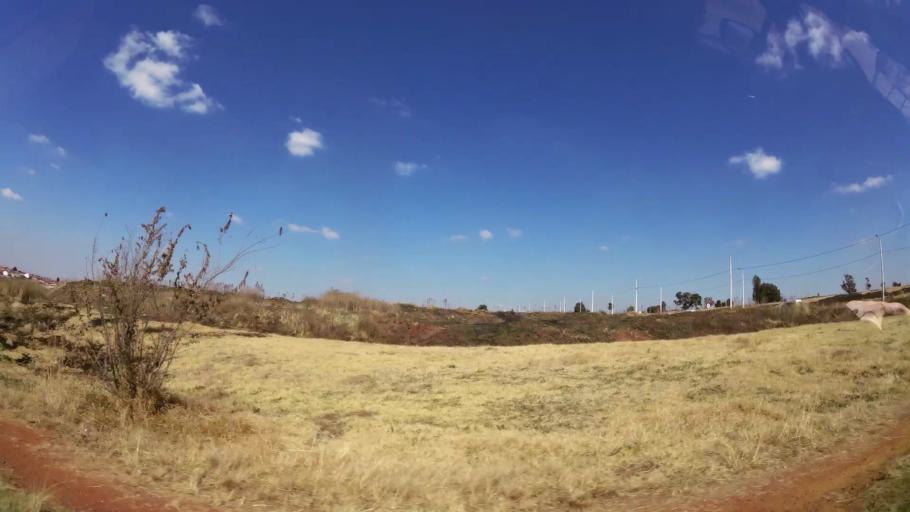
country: ZA
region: Gauteng
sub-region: West Rand District Municipality
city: Randfontein
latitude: -26.1559
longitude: 27.7632
